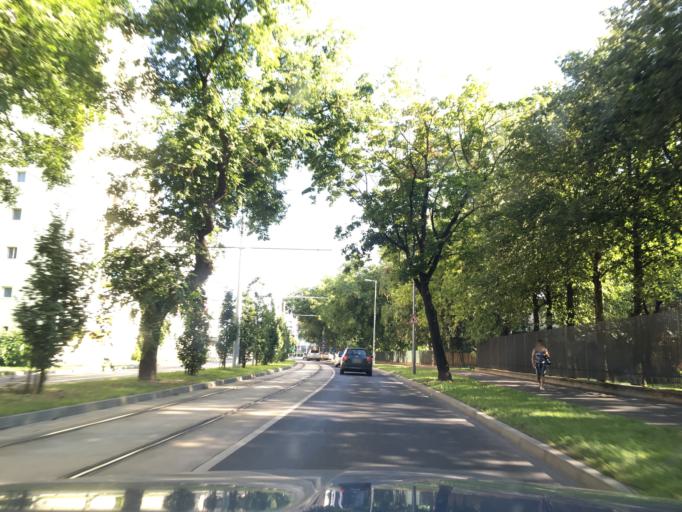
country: HU
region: Hajdu-Bihar
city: Debrecen
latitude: 47.5381
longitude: 21.6171
